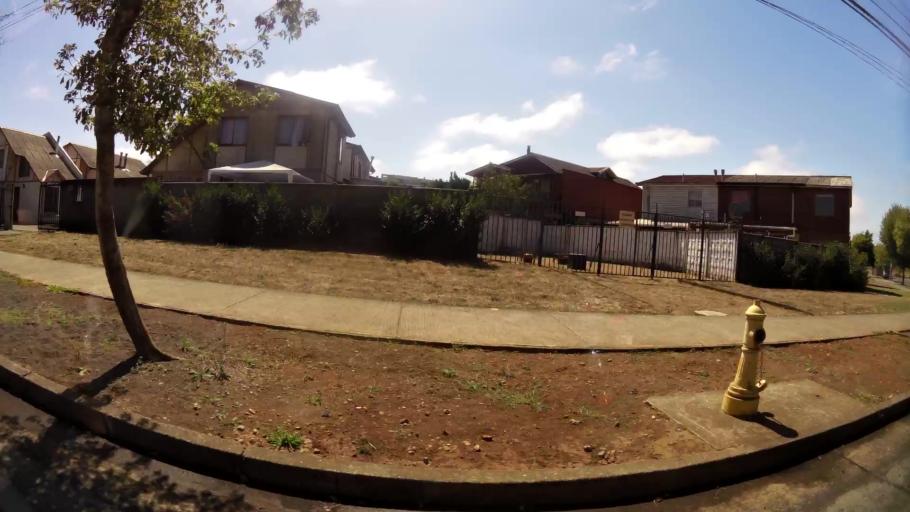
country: CL
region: Biobio
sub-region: Provincia de Concepcion
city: Concepcion
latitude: -36.7798
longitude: -73.0410
